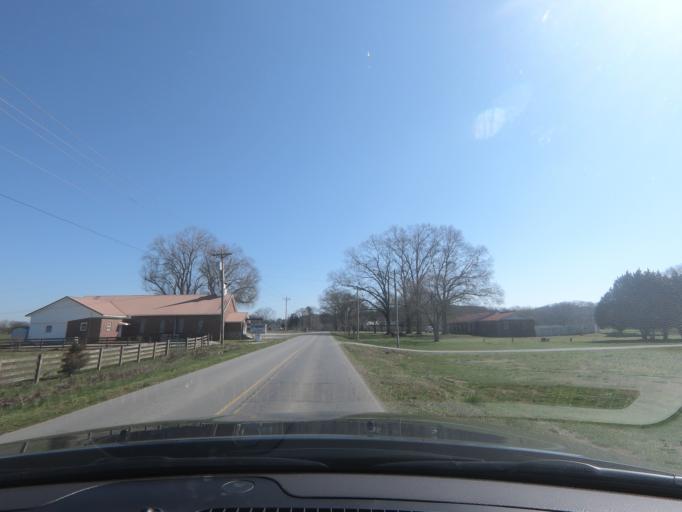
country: US
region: Georgia
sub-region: Gordon County
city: Calhoun
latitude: 34.4614
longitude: -85.0113
